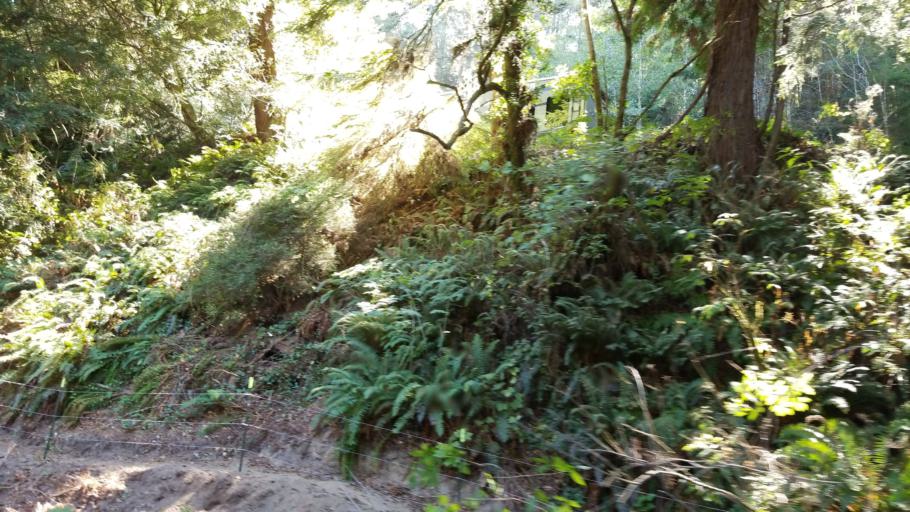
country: US
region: California
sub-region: Mendocino County
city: Fort Bragg
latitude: 39.4489
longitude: -123.7781
